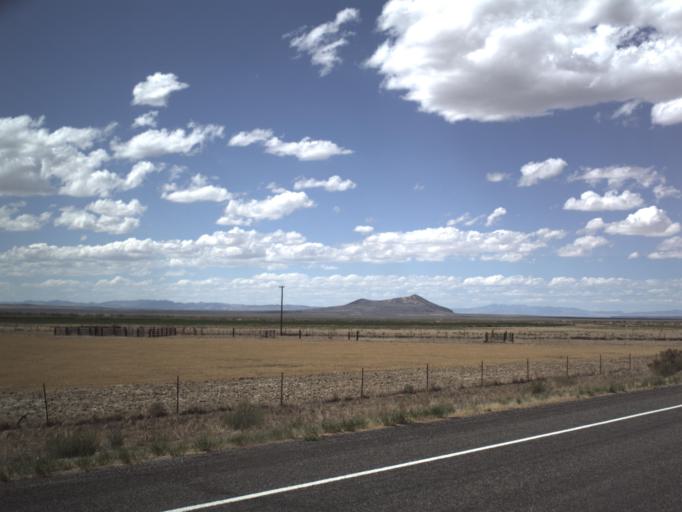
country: US
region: Utah
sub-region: Millard County
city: Fillmore
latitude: 39.1417
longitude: -112.3776
